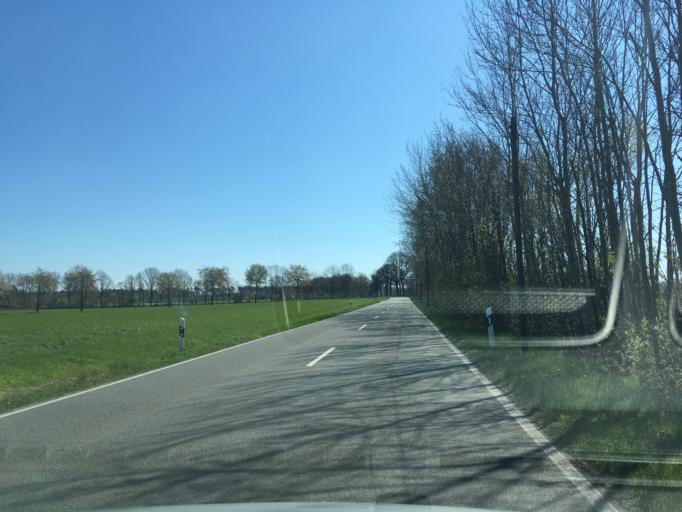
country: DE
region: North Rhine-Westphalia
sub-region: Regierungsbezirk Munster
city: Vreden
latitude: 52.0018
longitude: 6.8308
